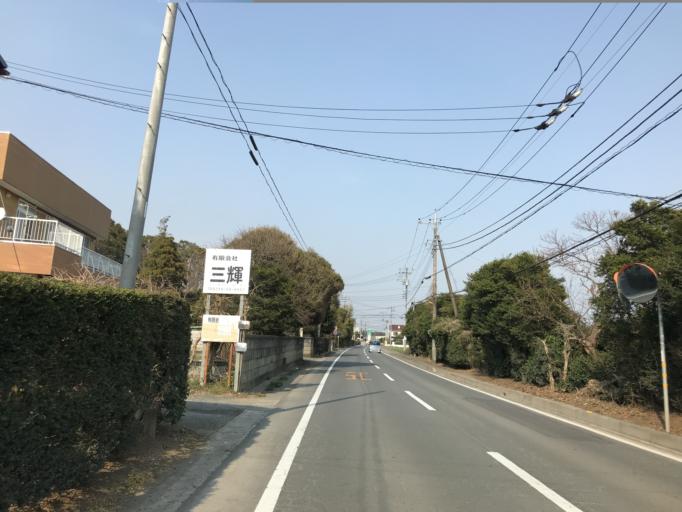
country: JP
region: Ibaraki
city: Okunoya
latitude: 36.1988
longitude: 140.3908
